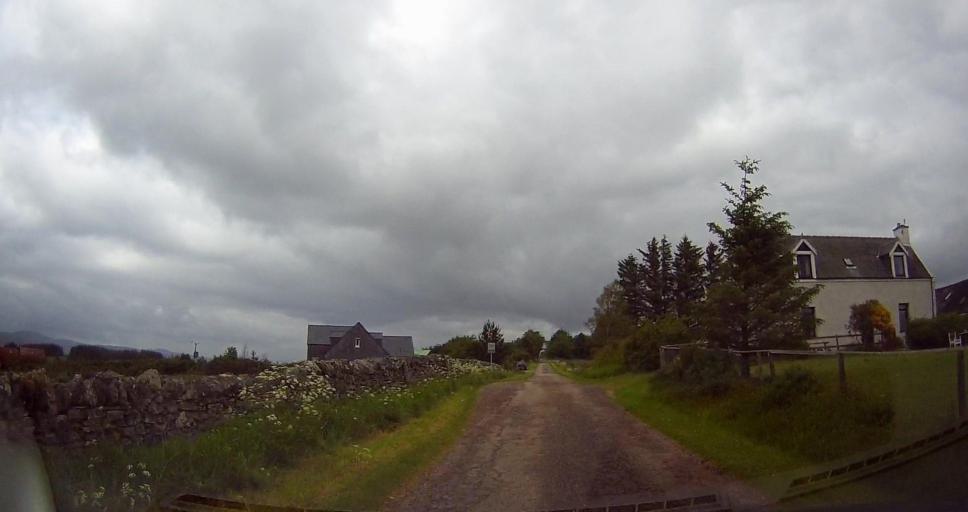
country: GB
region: Scotland
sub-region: Highland
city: Alness
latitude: 58.0739
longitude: -4.4384
